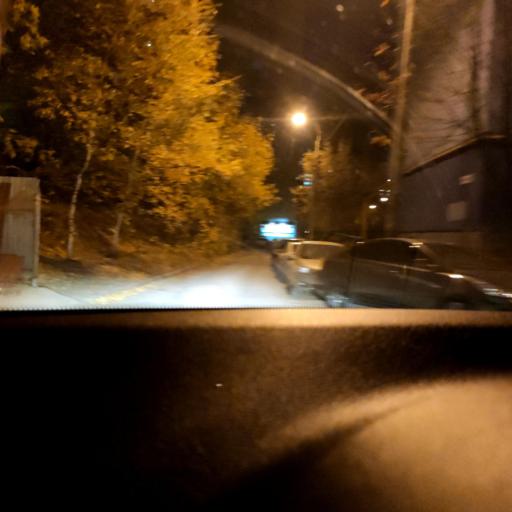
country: RU
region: Samara
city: Samara
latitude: 53.2624
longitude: 50.2135
